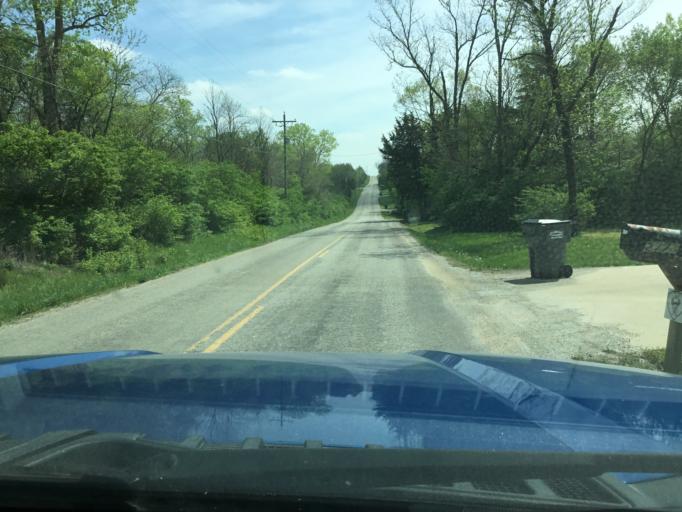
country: US
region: Kansas
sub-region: Shawnee County
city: Topeka
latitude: 39.1170
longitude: -95.5905
